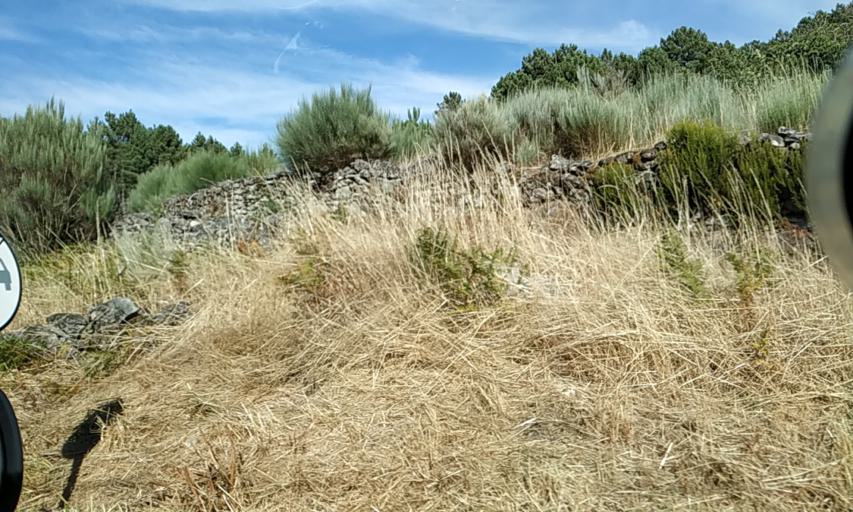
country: PT
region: Vila Real
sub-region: Sabrosa
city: Sabrosa
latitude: 41.3566
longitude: -7.5737
